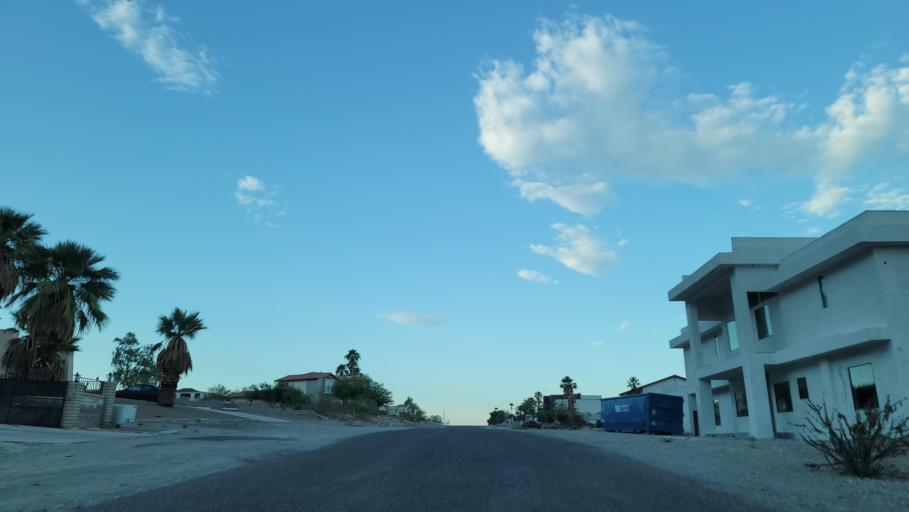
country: US
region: Nevada
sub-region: Clark County
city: Sunrise Manor
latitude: 36.1726
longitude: -115.0168
